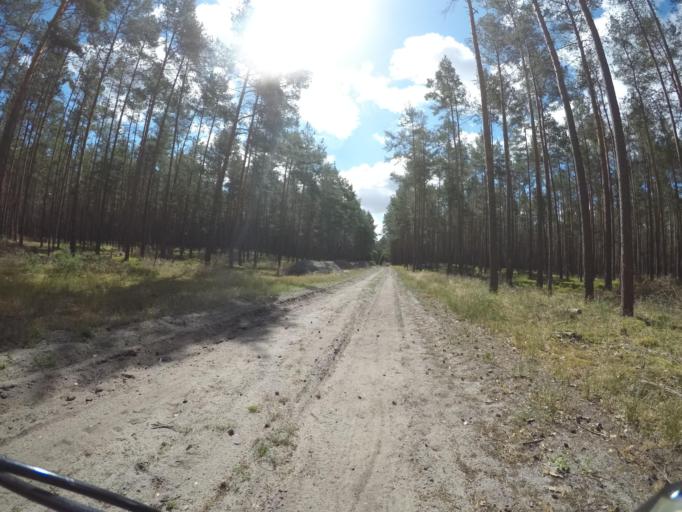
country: DE
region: Lower Saxony
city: Hitzacker
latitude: 53.2212
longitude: 11.0385
